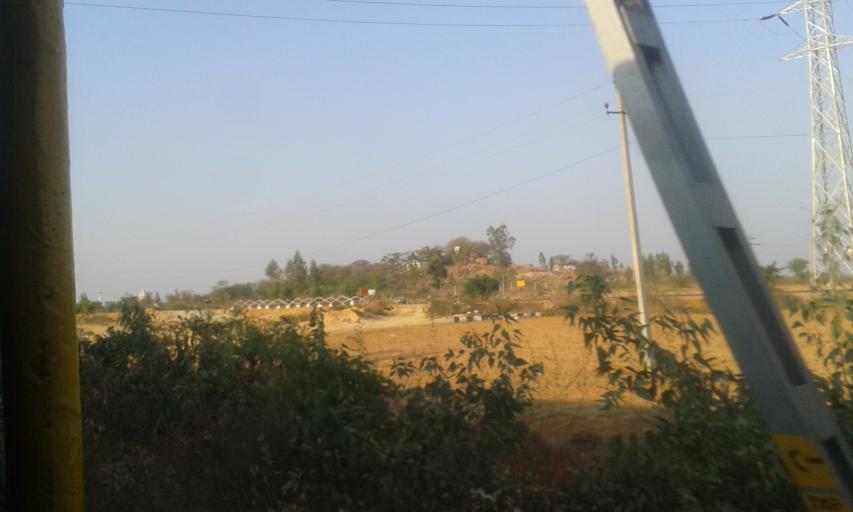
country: IN
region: Karnataka
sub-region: Chikkaballapur
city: Gauribidanur
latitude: 13.5686
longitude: 77.5092
